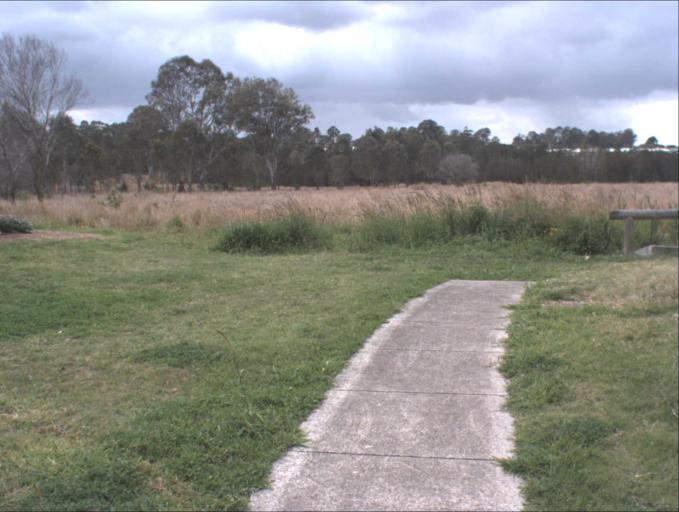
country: AU
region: Queensland
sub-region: Logan
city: Waterford West
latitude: -27.6935
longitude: 153.1140
